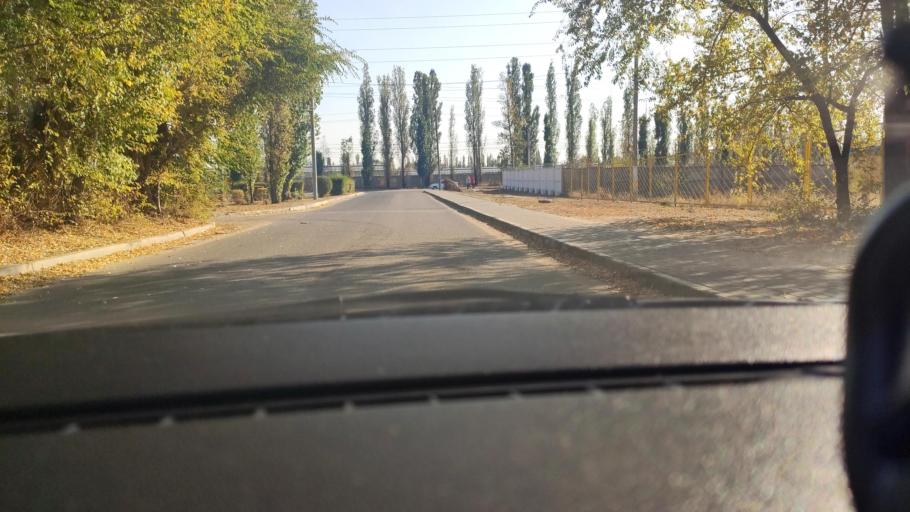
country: RU
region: Voronezj
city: Pridonskoy
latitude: 51.6232
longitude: 39.0691
